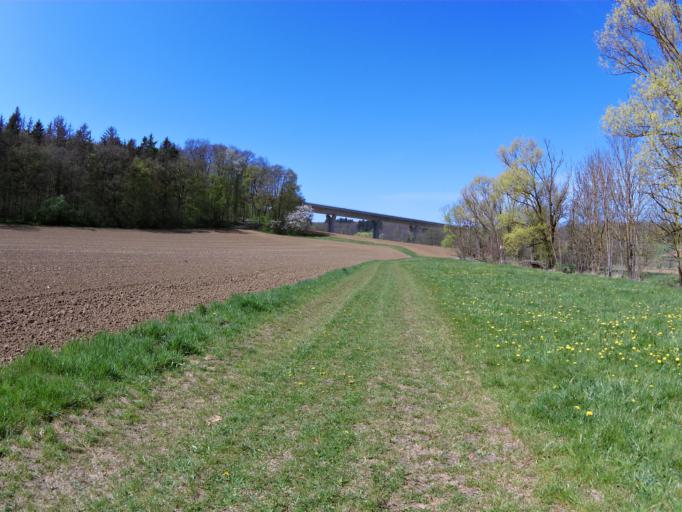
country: DE
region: Bavaria
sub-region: Regierungsbezirk Unterfranken
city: Estenfeld
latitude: 49.8573
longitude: 10.0000
